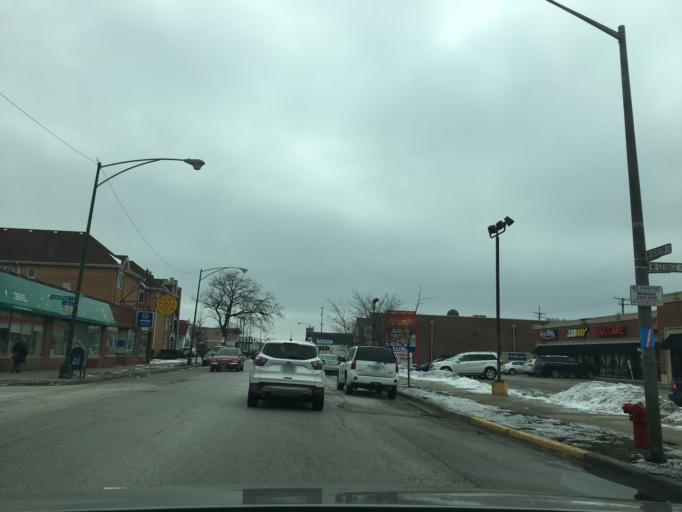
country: US
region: Illinois
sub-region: Cook County
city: Elmwood Park
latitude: 41.9327
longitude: -87.8066
